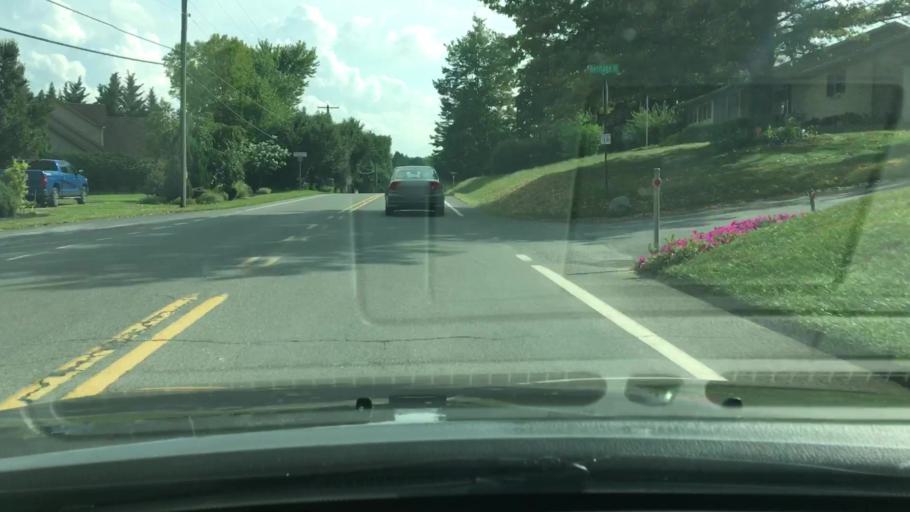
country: US
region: Pennsylvania
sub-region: Franklin County
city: Guilford
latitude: 39.9256
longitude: -77.5913
